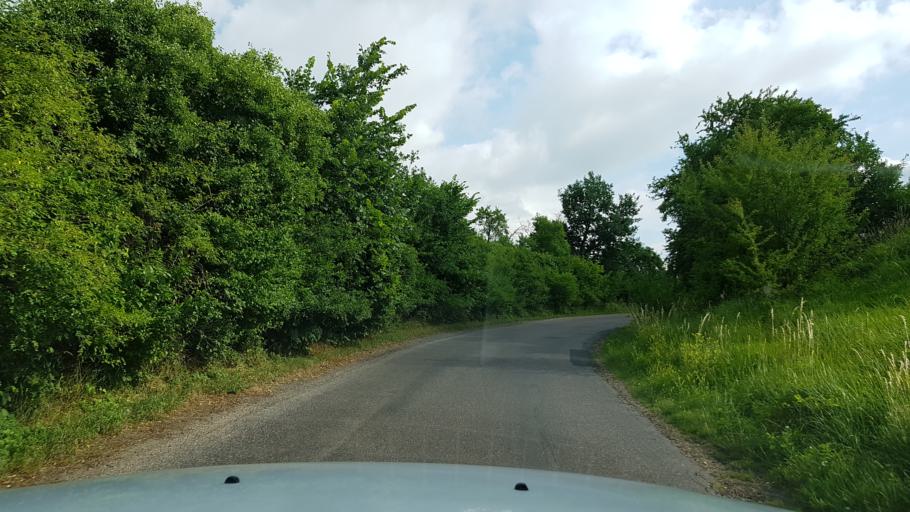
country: PL
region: West Pomeranian Voivodeship
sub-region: Powiat gryfinski
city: Gryfino
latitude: 53.2143
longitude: 14.5946
